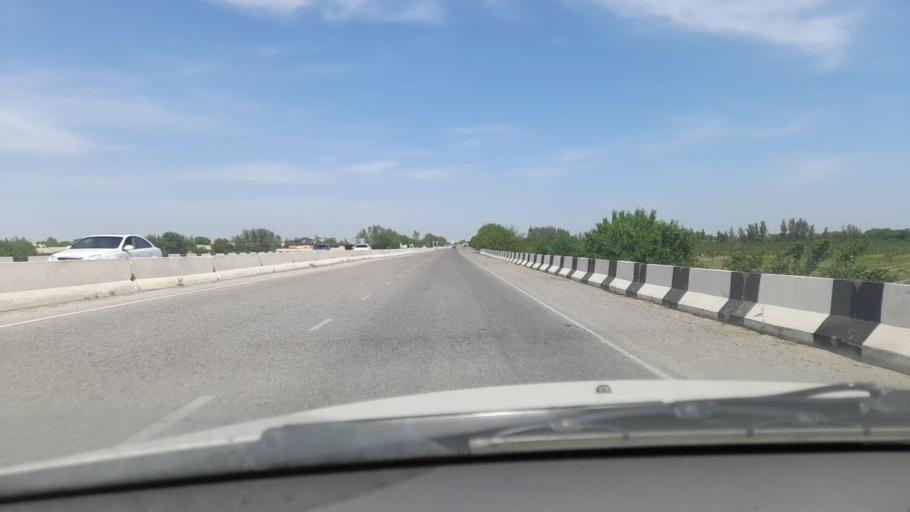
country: UZ
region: Samarqand
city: Kattaqo'rg'on
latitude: 39.9327
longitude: 66.3661
